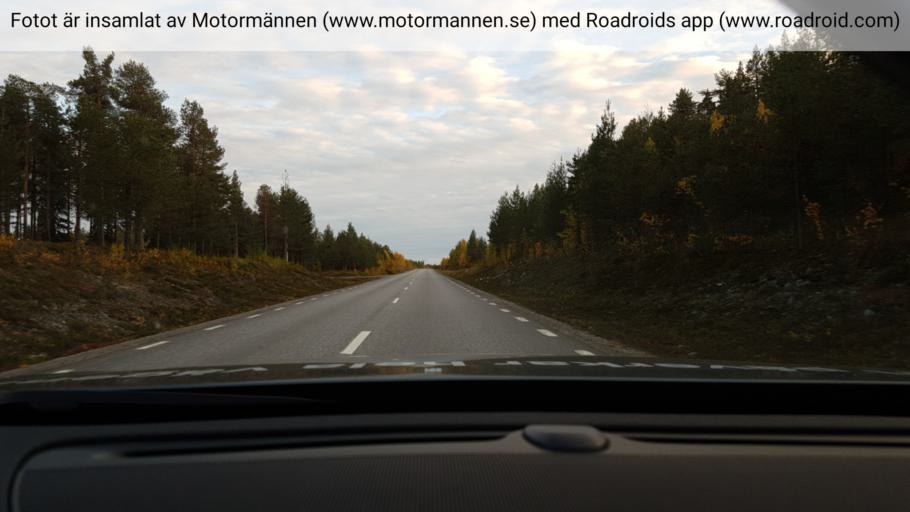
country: SE
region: Norrbotten
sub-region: Jokkmokks Kommun
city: Jokkmokk
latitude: 66.4229
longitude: 19.6828
